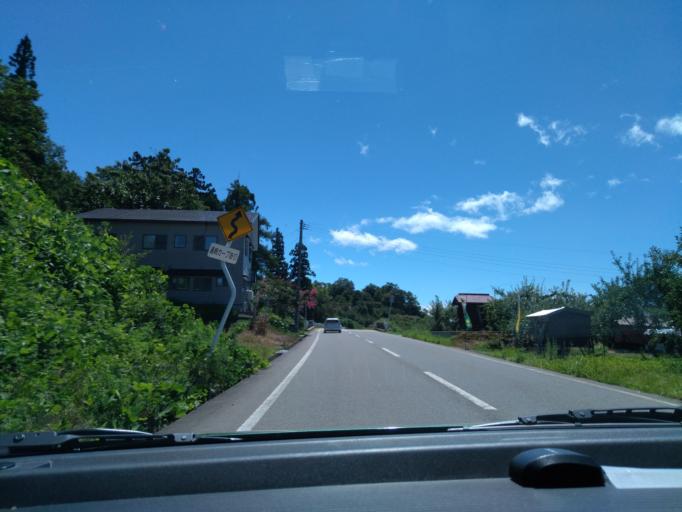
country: JP
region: Akita
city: Yokotemachi
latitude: 39.2294
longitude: 140.5646
